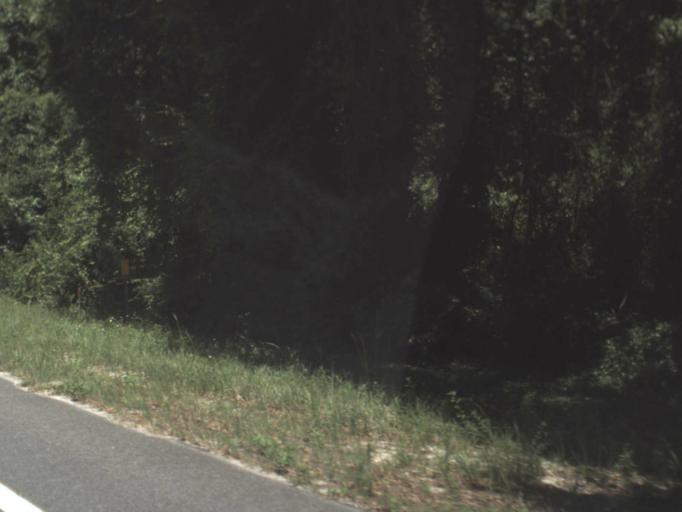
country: US
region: Florida
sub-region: Dixie County
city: Cross City
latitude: 29.7790
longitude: -82.9769
